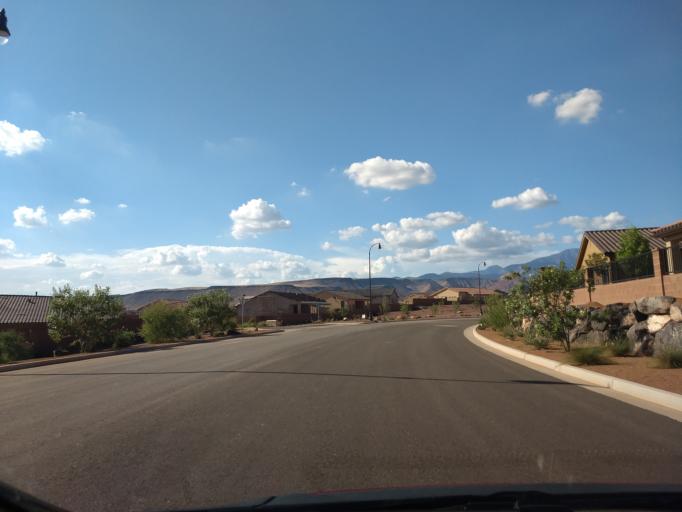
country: US
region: Utah
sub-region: Washington County
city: Washington
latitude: 37.1431
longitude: -113.5154
